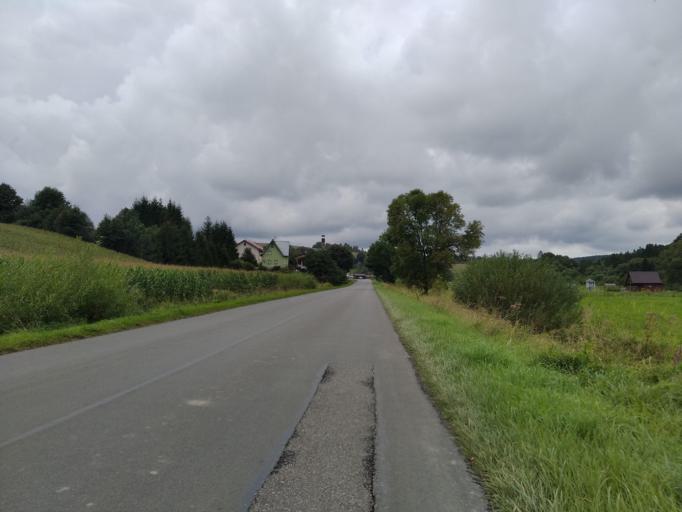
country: PL
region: Subcarpathian Voivodeship
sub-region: Powiat przemyski
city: Bircza
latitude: 49.7008
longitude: 22.3726
